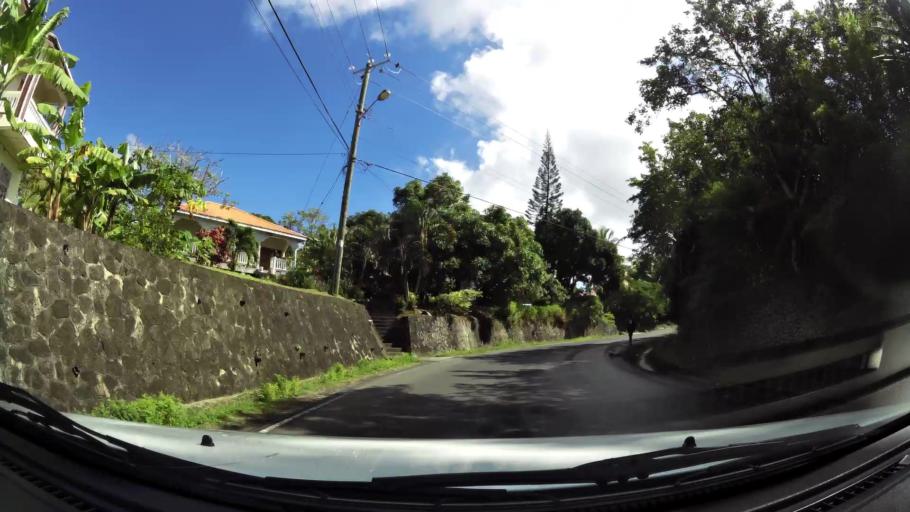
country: LC
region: Choiseul Quarter
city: Choiseul
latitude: 13.7756
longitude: -61.0337
